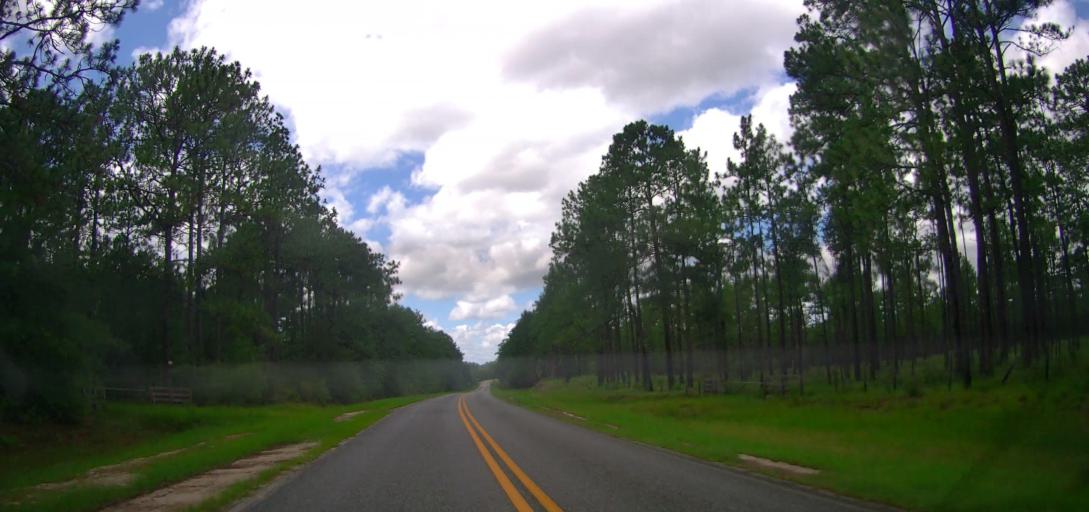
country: US
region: Georgia
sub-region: Turner County
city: Ashburn
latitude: 31.6999
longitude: -83.4996
